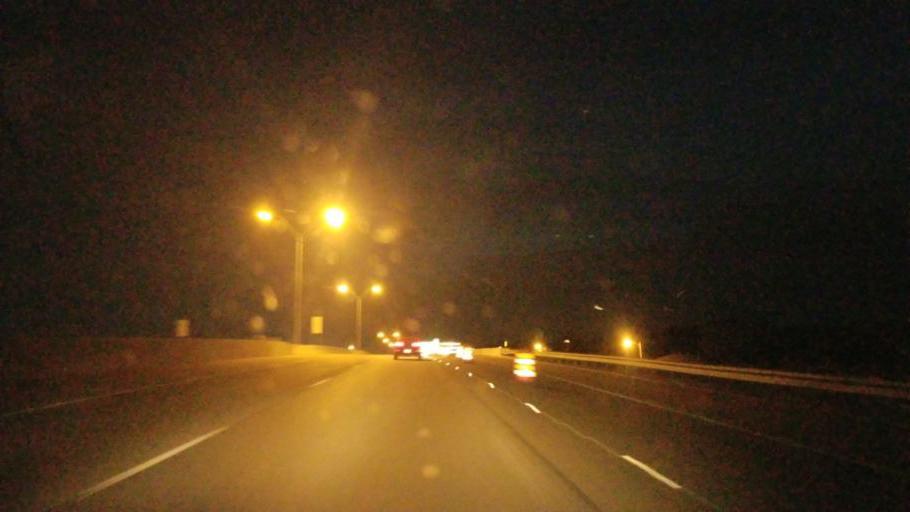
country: US
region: Texas
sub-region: Potter County
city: Amarillo
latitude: 35.1954
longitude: -101.8569
